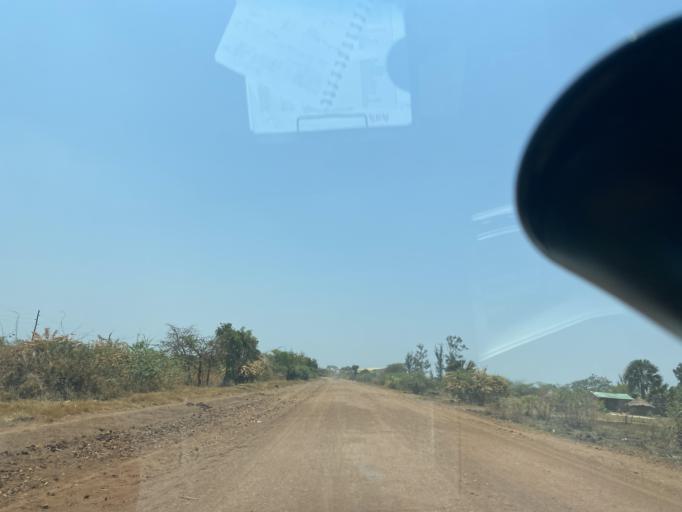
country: ZM
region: Southern
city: Nakambala
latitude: -15.4730
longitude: 27.8975
